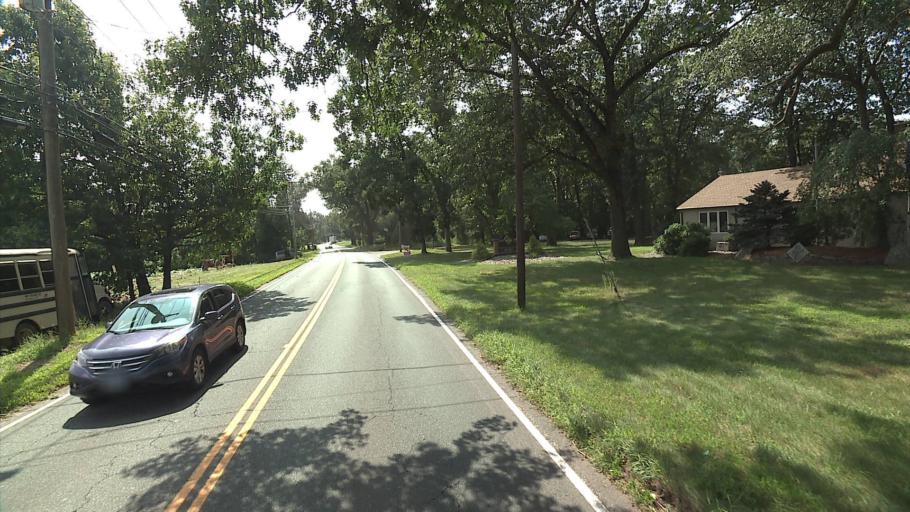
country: US
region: Connecticut
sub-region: Hartford County
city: Broad Brook
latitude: 41.9309
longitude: -72.5351
